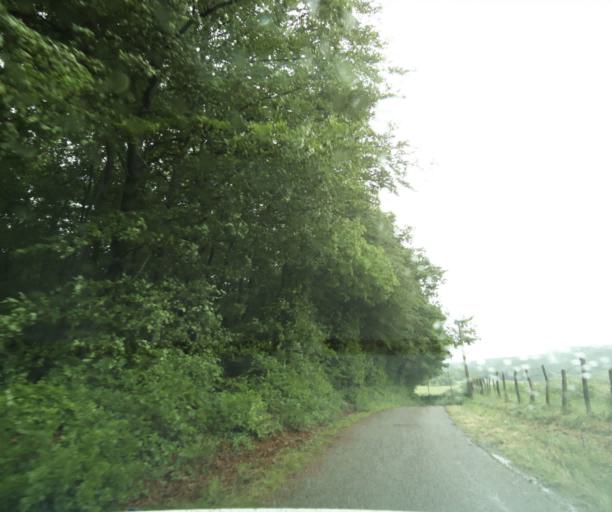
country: FR
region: Bourgogne
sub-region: Departement de Saone-et-Loire
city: Charolles
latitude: 46.4939
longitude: 4.4073
